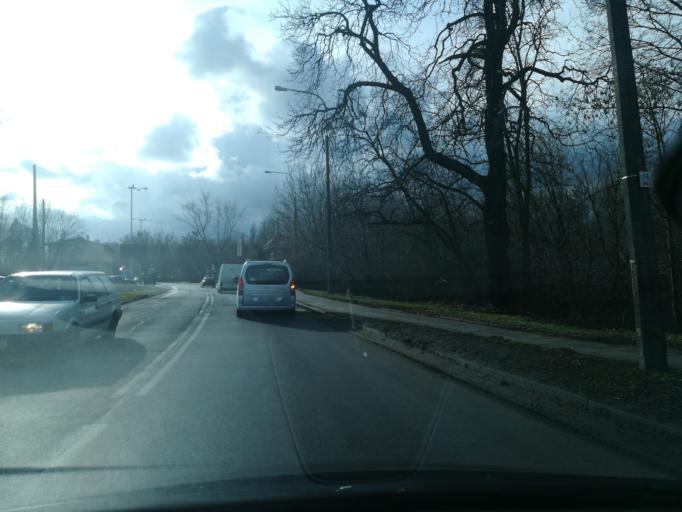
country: PL
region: Kujawsko-Pomorskie
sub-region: Torun
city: Torun
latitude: 53.0020
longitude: 18.6160
